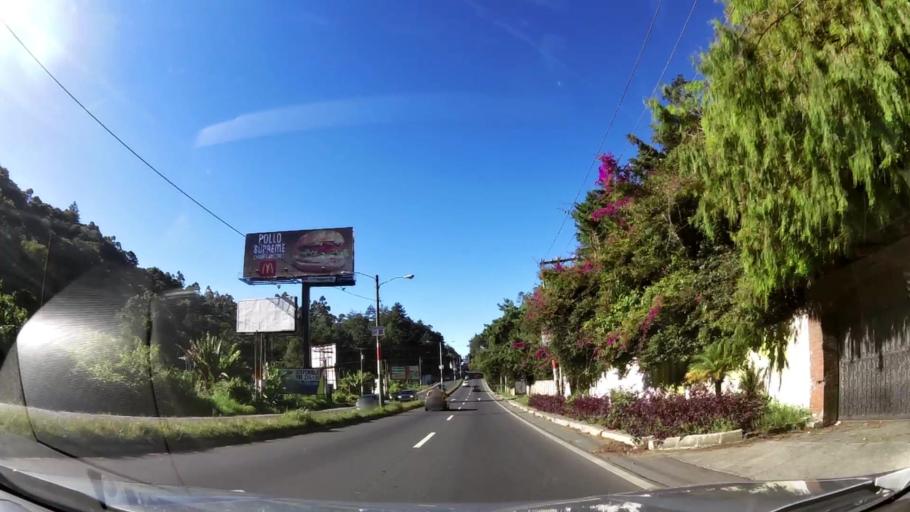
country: GT
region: Guatemala
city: Santa Catarina Pinula
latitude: 14.5331
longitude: -90.4611
